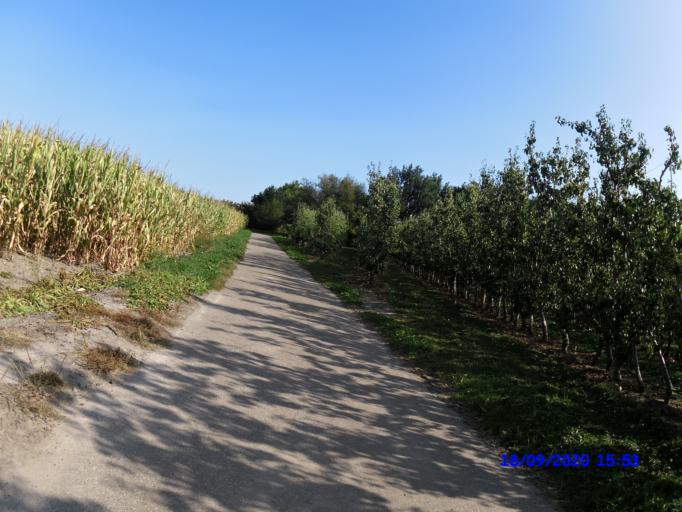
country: BE
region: Flanders
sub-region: Provincie Limburg
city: Gingelom
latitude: 50.7384
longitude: 5.1428
